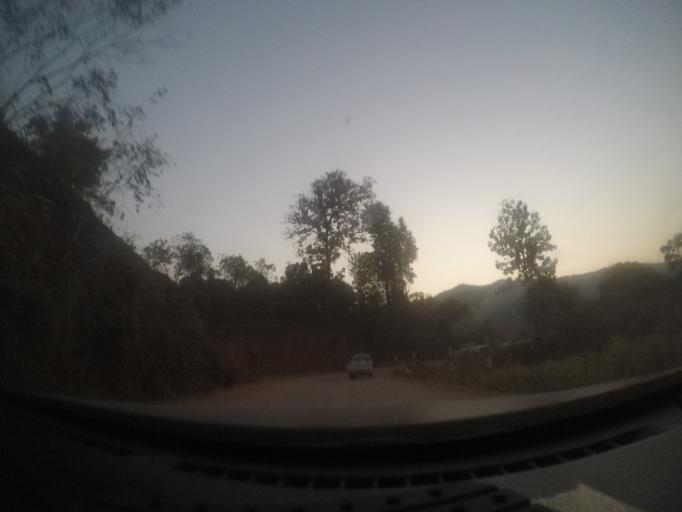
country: MM
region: Mandalay
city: Yamethin
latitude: 20.6971
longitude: 96.5042
